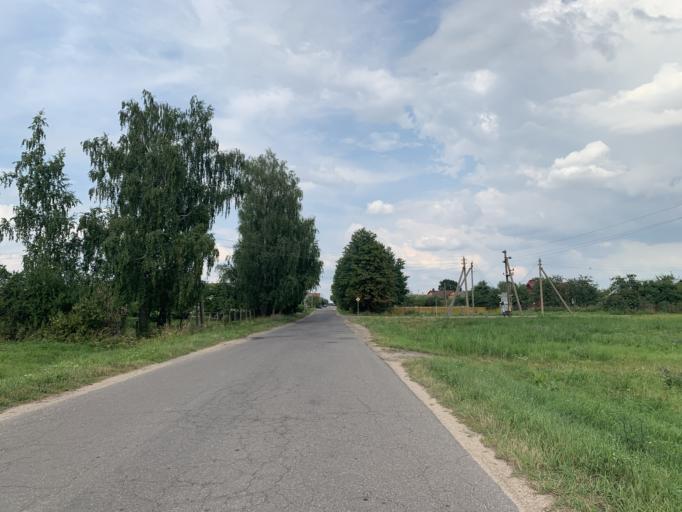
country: BY
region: Minsk
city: Nyasvizh
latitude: 53.2054
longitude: 26.6818
